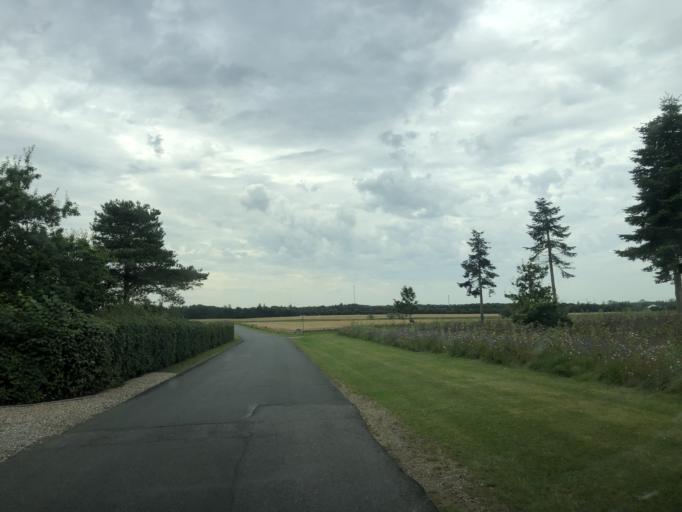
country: DK
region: Central Jutland
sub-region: Holstebro Kommune
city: Holstebro
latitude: 56.3836
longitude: 8.5207
